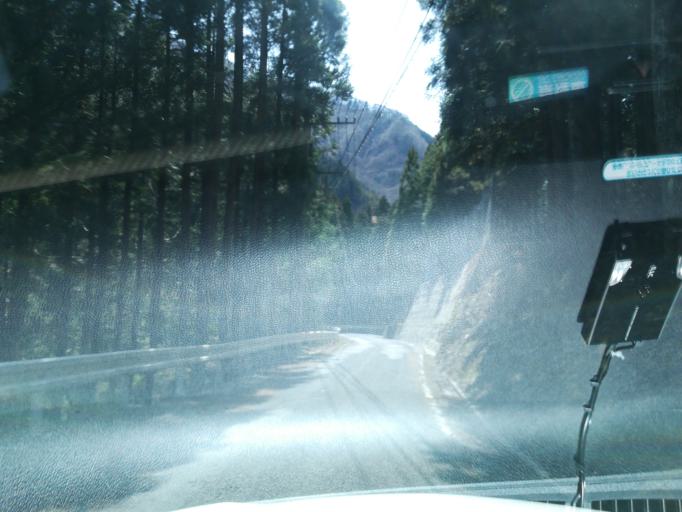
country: JP
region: Tokushima
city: Wakimachi
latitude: 33.8589
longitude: 134.0596
